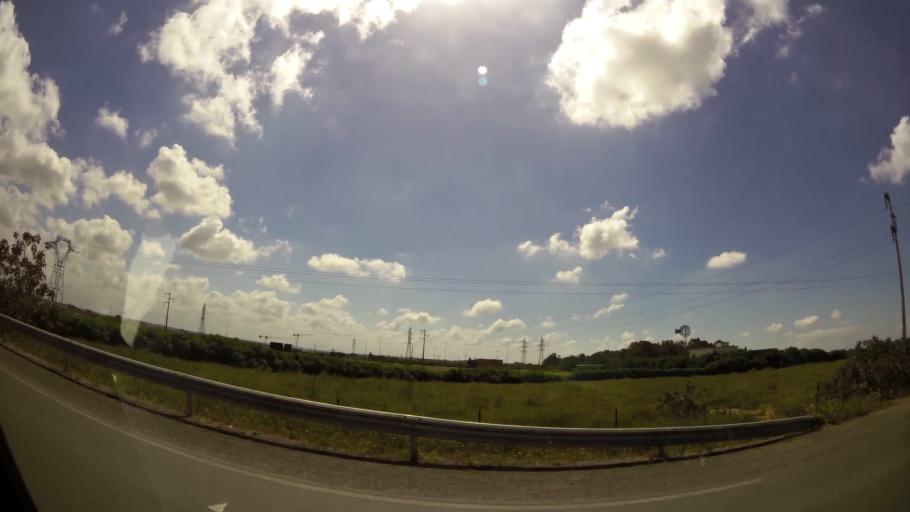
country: MA
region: Grand Casablanca
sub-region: Nouaceur
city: Bouskoura
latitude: 33.5032
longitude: -7.6087
